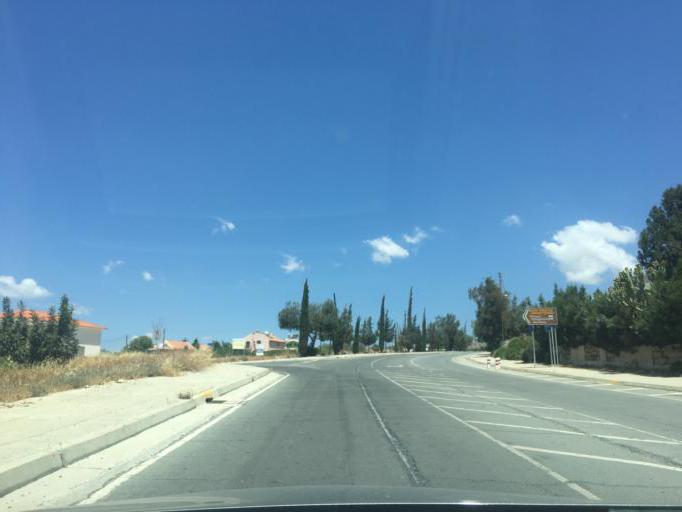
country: CY
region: Limassol
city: Mouttagiaka
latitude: 34.7234
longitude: 33.0643
